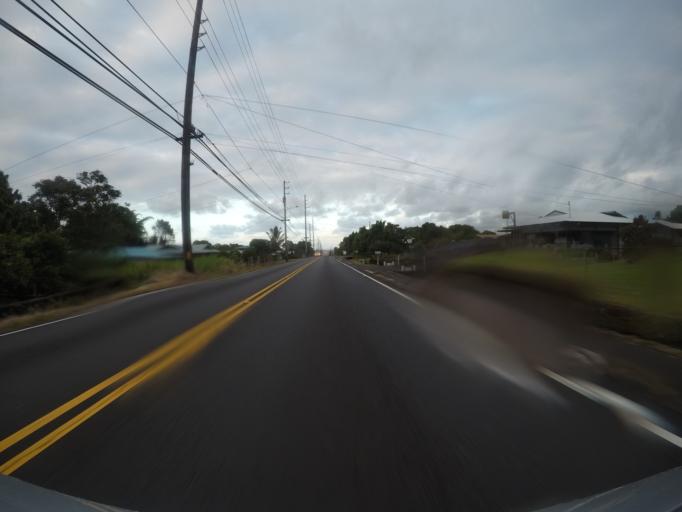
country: US
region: Hawaii
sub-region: Hawaii County
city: Hilo
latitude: 19.6833
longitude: -155.0870
